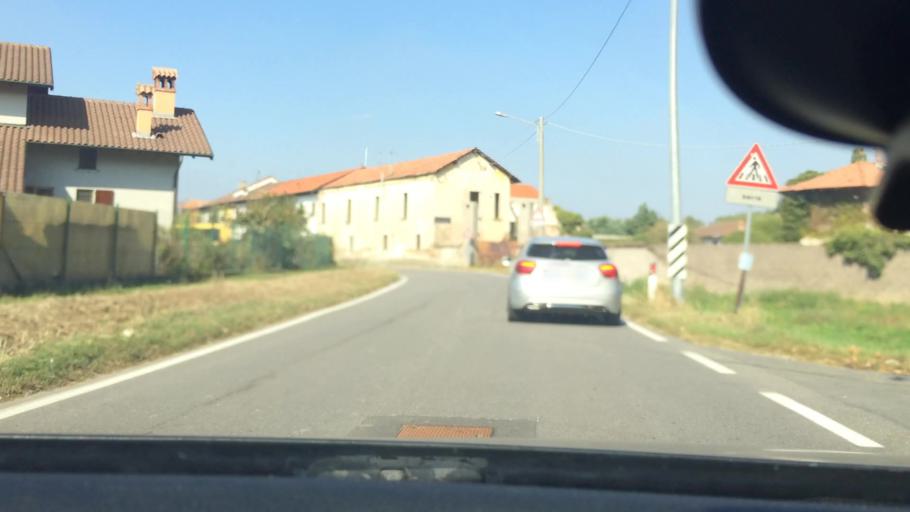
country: IT
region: Lombardy
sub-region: Citta metropolitana di Milano
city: Casate
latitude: 45.4911
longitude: 8.8297
